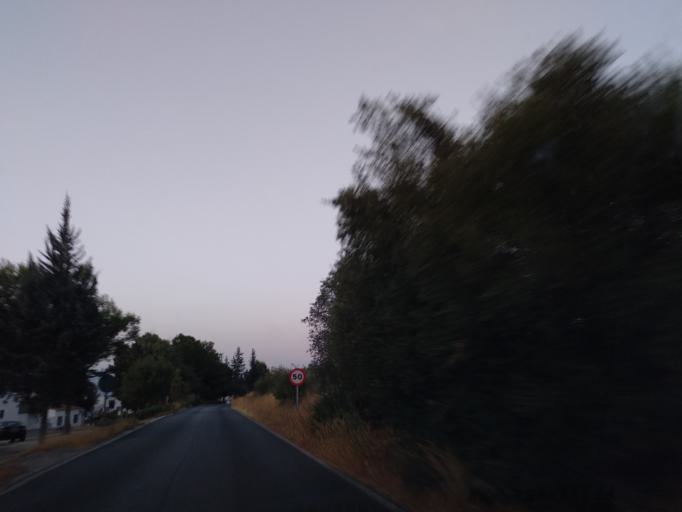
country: ES
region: Andalusia
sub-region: Provincia de Malaga
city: Cartama
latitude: 36.7044
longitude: -4.6422
